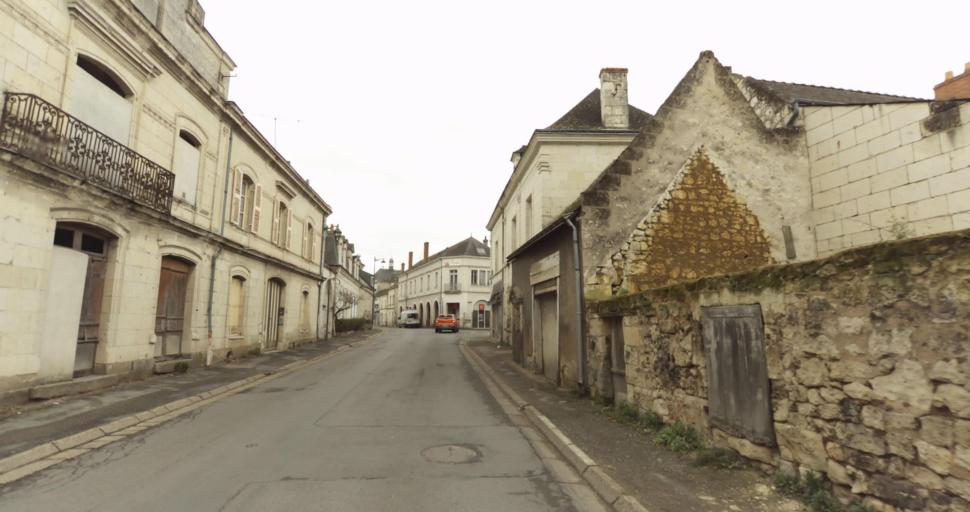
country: FR
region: Pays de la Loire
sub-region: Departement de Maine-et-Loire
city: Allonnes
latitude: 47.2936
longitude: 0.0222
